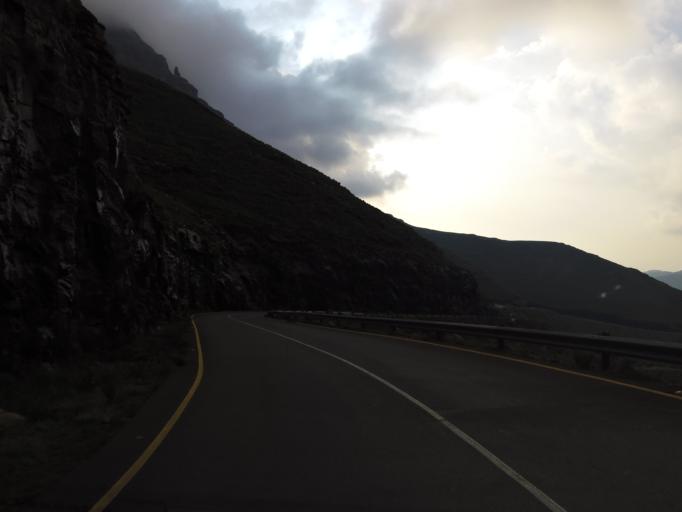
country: LS
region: Butha-Buthe
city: Butha-Buthe
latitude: -29.0712
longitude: 28.3761
